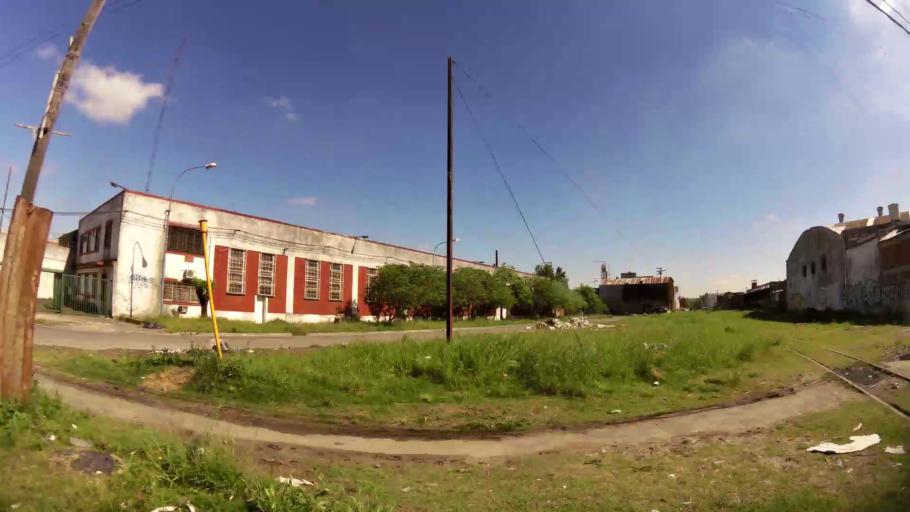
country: AR
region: Buenos Aires
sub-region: Partido de Lanus
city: Lanus
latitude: -34.6695
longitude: -58.4189
